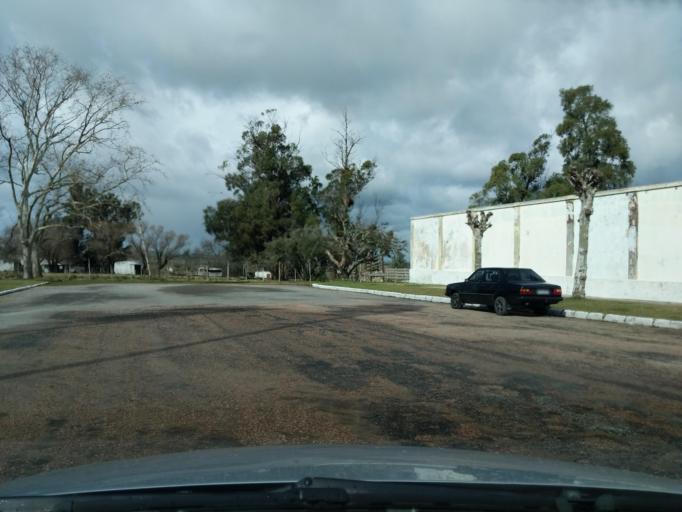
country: UY
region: Florida
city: Florida
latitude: -34.1088
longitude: -56.2288
